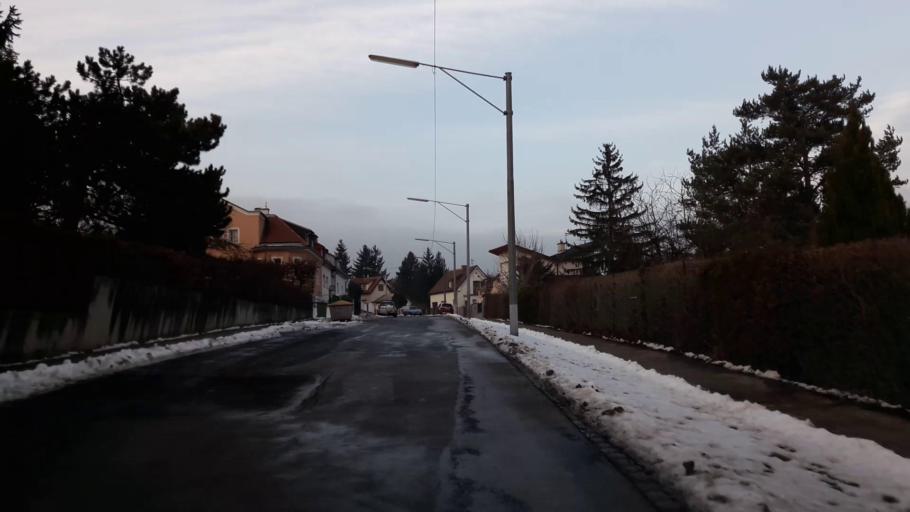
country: AT
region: Lower Austria
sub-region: Politischer Bezirk Wien-Umgebung
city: Purkersdorf
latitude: 48.2146
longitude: 16.2477
